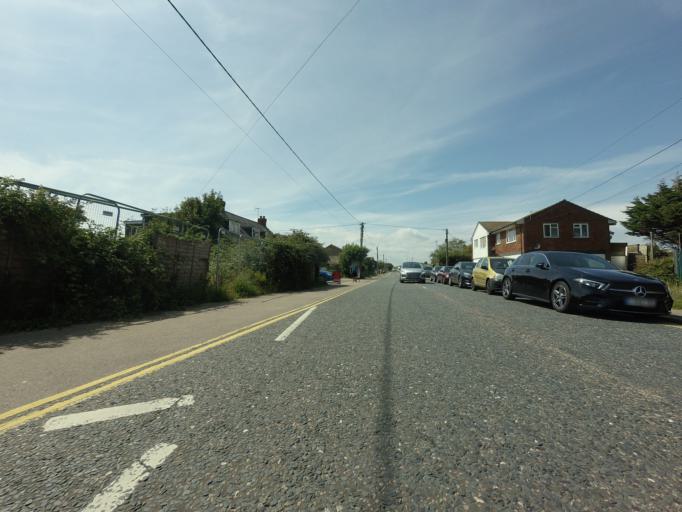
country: GB
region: England
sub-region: East Sussex
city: Rye
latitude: 50.9350
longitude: 0.7981
